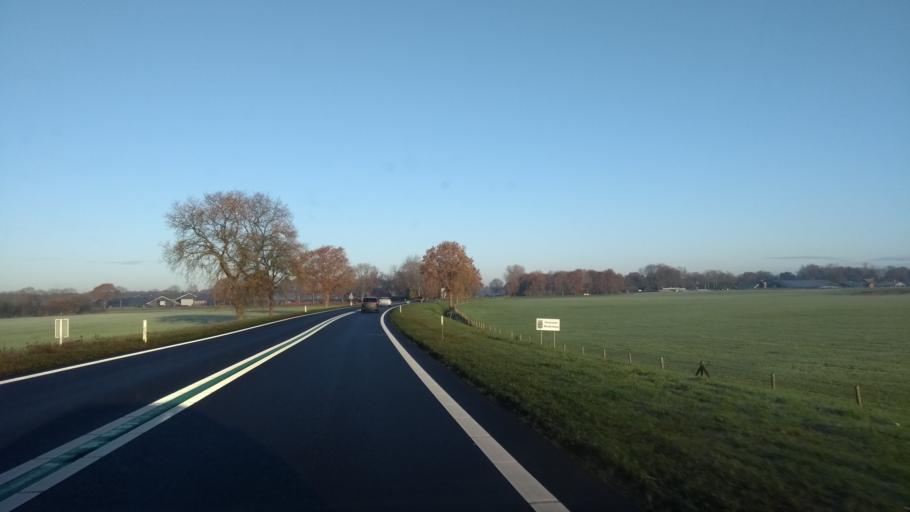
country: NL
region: Overijssel
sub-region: Gemeente Twenterand
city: Vroomshoop
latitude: 52.5165
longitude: 6.5579
